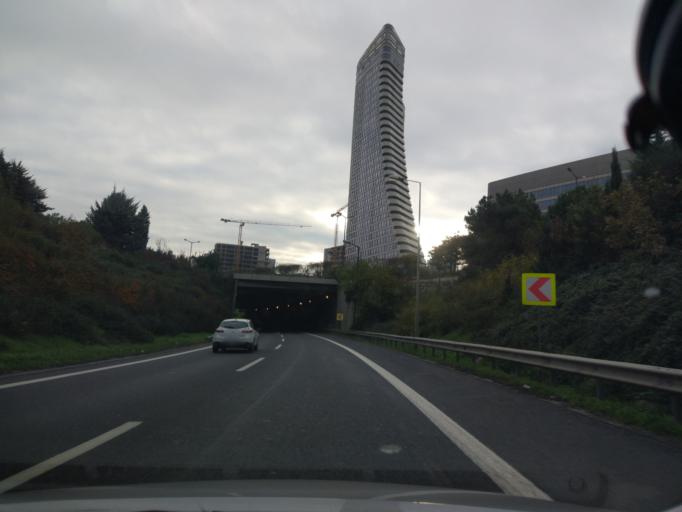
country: TR
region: Istanbul
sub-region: Atasehir
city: Atasehir
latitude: 40.9964
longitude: 29.1217
